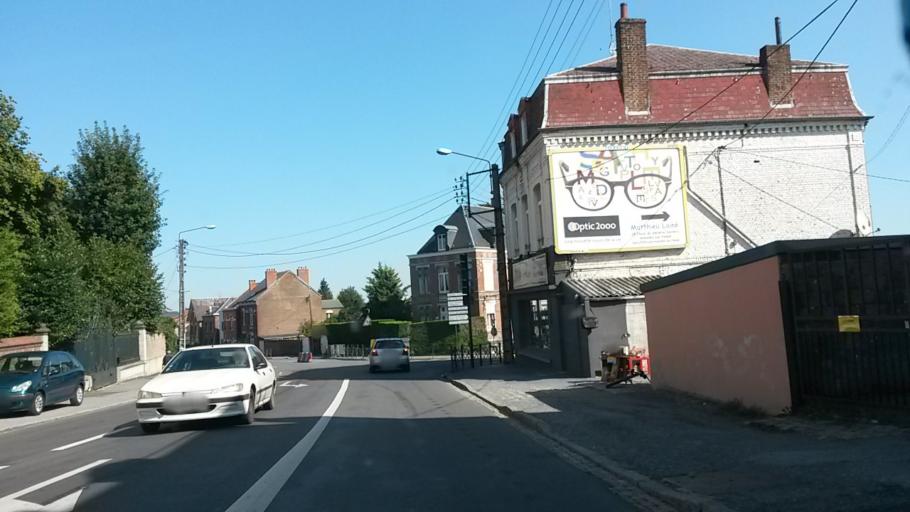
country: FR
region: Nord-Pas-de-Calais
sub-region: Departement du Nord
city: Avesnes-sur-Helpe
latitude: 50.1199
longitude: 3.9261
